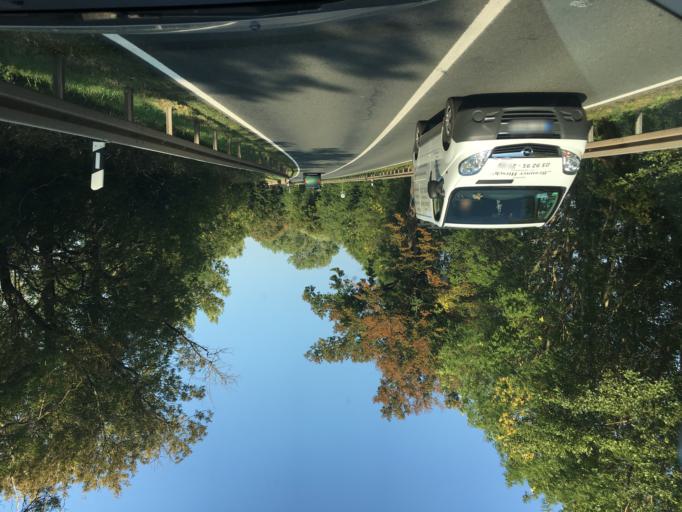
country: DE
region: Saxony-Anhalt
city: Calbe
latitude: 51.9426
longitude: 11.7613
